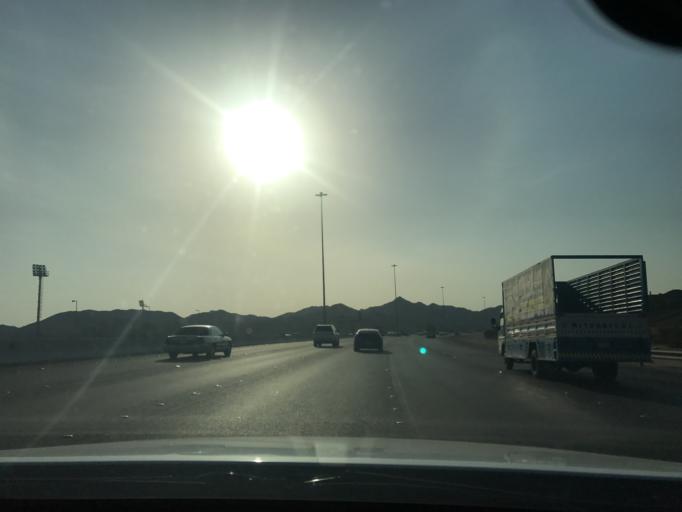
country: SA
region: Makkah
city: Jeddah
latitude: 21.3900
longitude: 39.4177
